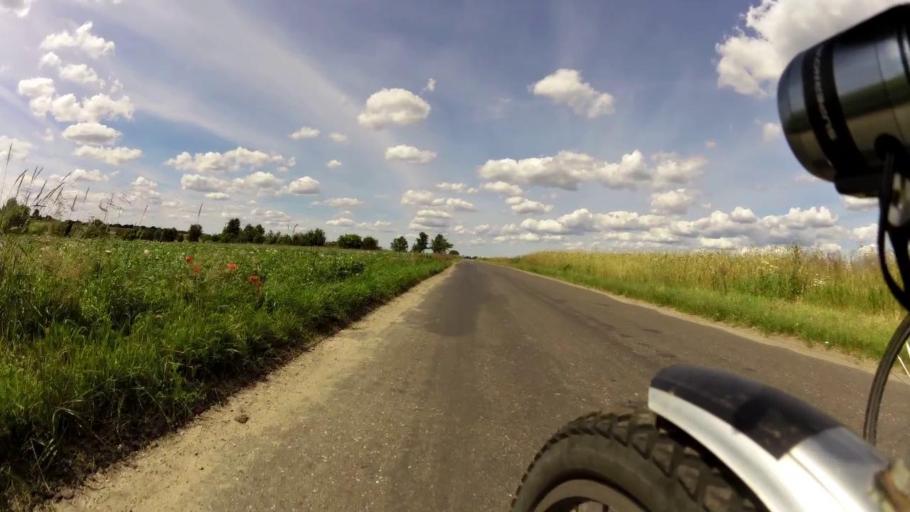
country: PL
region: West Pomeranian Voivodeship
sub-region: Powiat stargardzki
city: Chociwel
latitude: 53.5390
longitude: 15.4318
